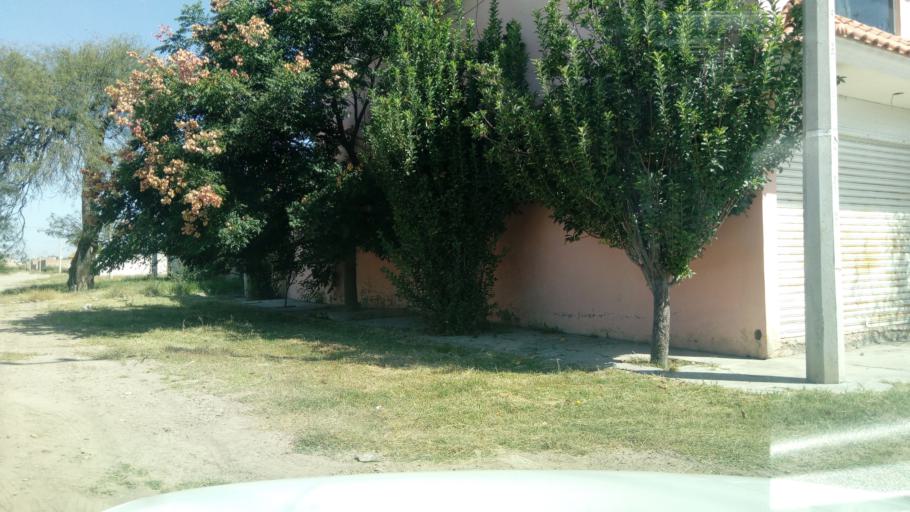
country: MX
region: Durango
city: Victoria de Durango
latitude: 23.9829
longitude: -104.6708
